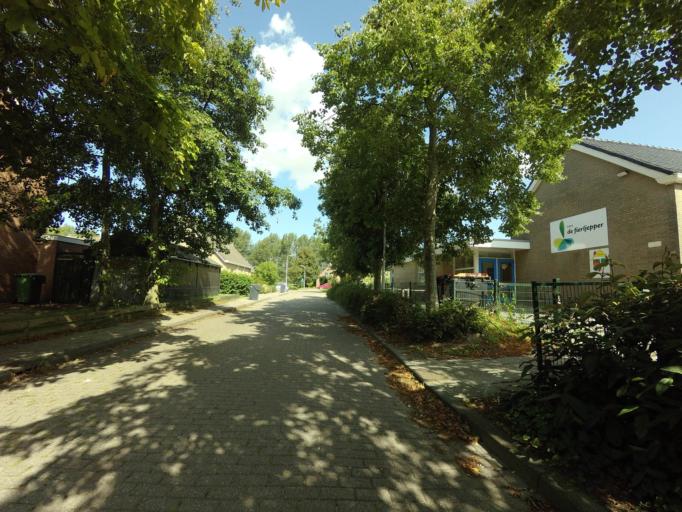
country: NL
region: Friesland
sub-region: Gemeente Het Bildt
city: Sint Annaparochie
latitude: 53.2806
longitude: 5.7018
